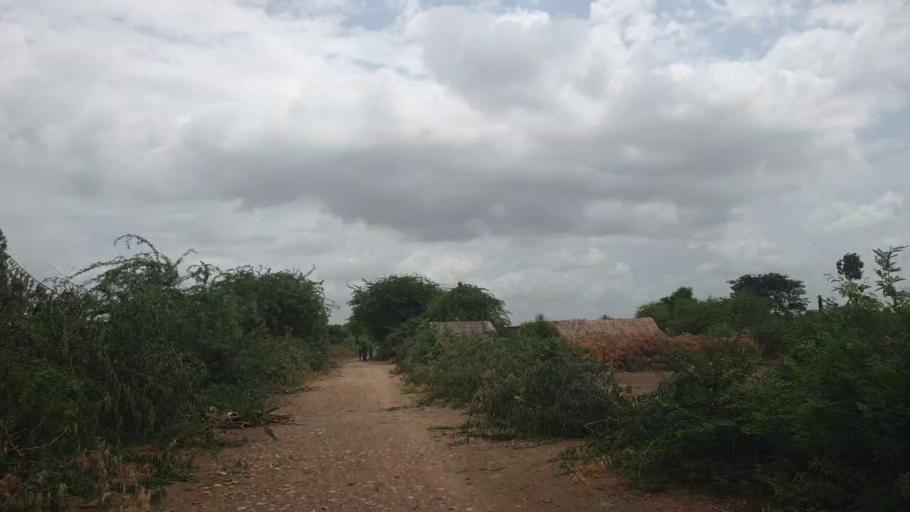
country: PK
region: Sindh
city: Badin
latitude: 24.6352
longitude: 68.9486
